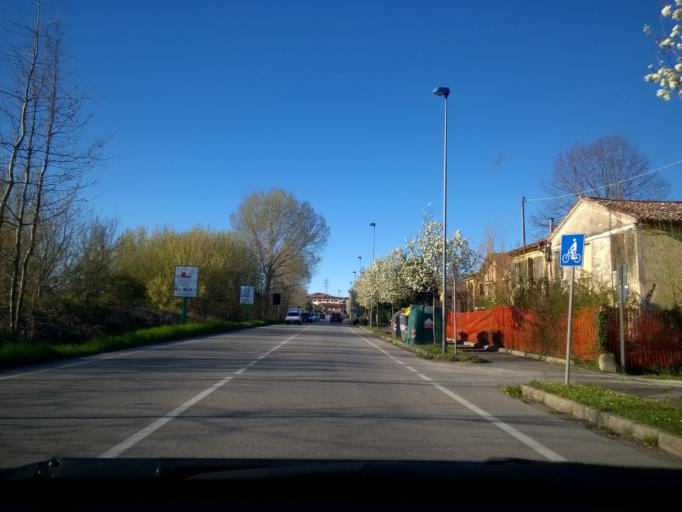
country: IT
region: Veneto
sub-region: Provincia di Venezia
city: Mirano
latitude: 45.4902
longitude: 12.1015
